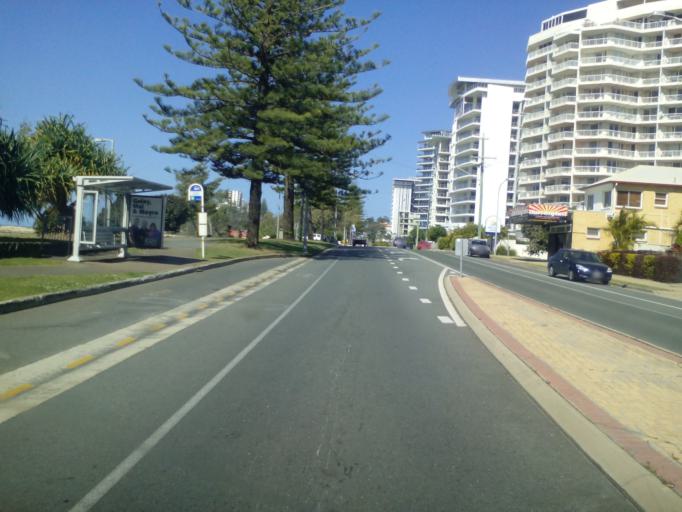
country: AU
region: New South Wales
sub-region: Tweed
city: Tweed Heads West
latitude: -28.1668
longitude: 153.5248
